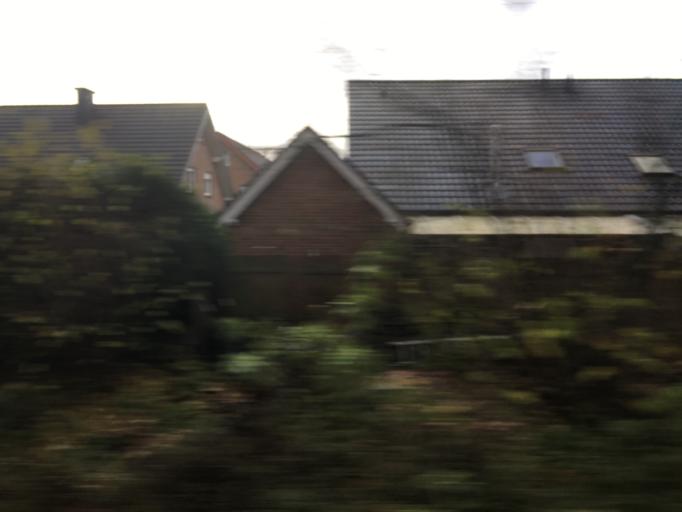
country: DE
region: North Rhine-Westphalia
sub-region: Regierungsbezirk Munster
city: Steinfurt
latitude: 52.1239
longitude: 7.3733
